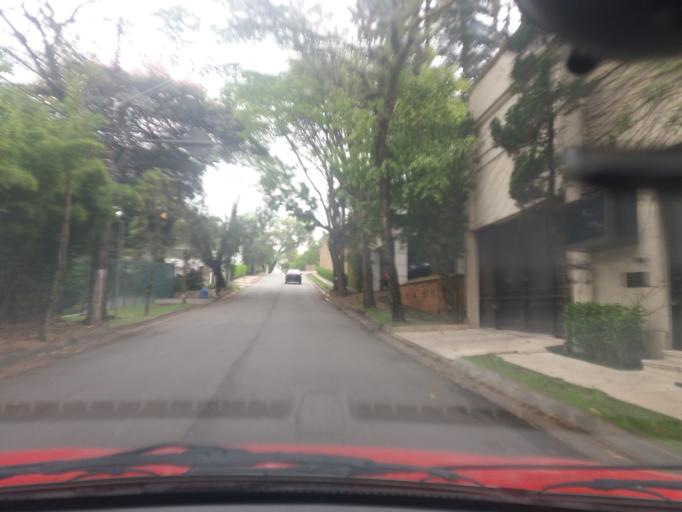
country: BR
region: Sao Paulo
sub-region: Sao Paulo
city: Sao Paulo
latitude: -23.5938
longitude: -46.7079
